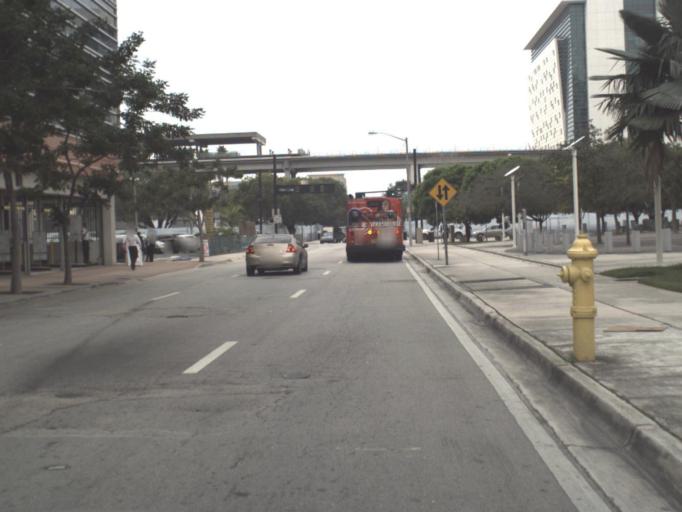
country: US
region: Florida
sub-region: Miami-Dade County
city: Miami
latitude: 25.7771
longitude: -80.1942
